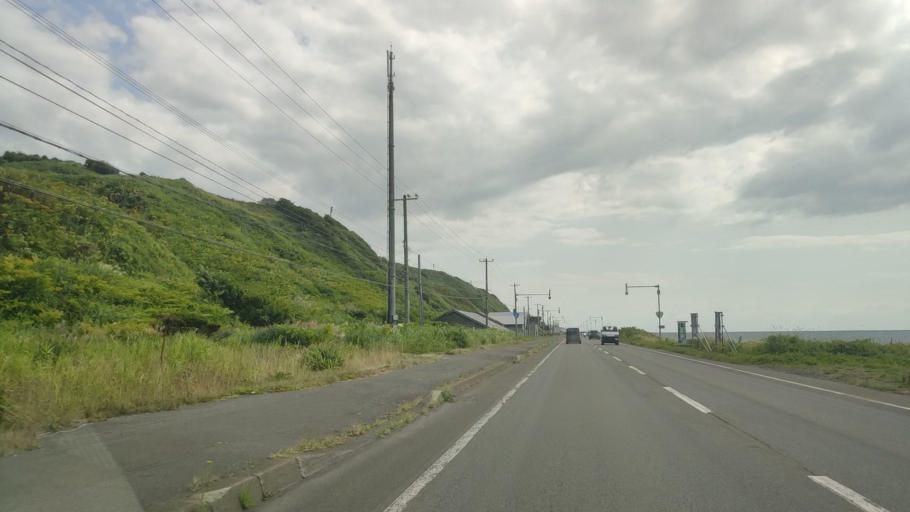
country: JP
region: Hokkaido
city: Rumoi
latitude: 44.2018
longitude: 141.6580
